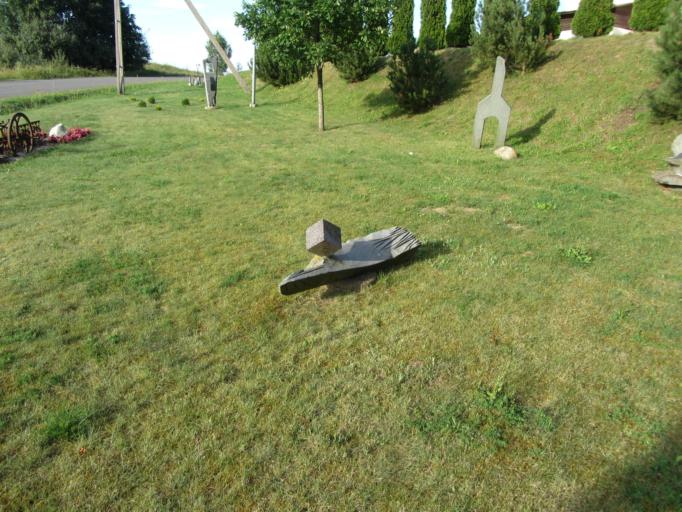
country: LT
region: Utenos apskritis
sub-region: Utena
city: Utena
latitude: 55.3949
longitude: 25.6751
